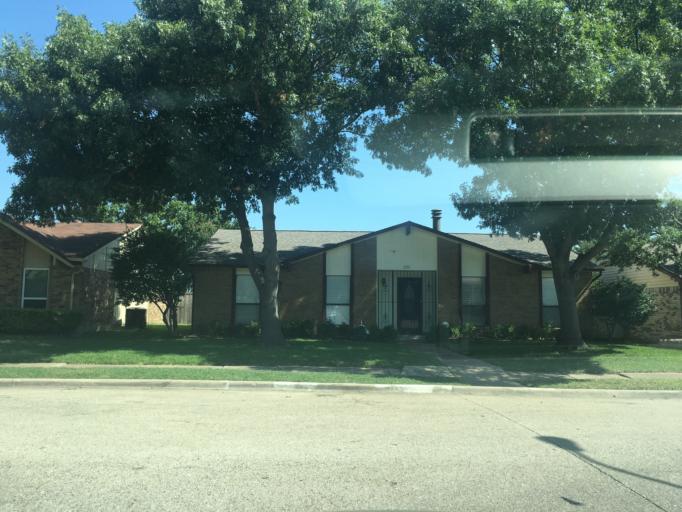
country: US
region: Texas
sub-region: Dallas County
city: Garland
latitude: 32.8563
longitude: -96.6636
